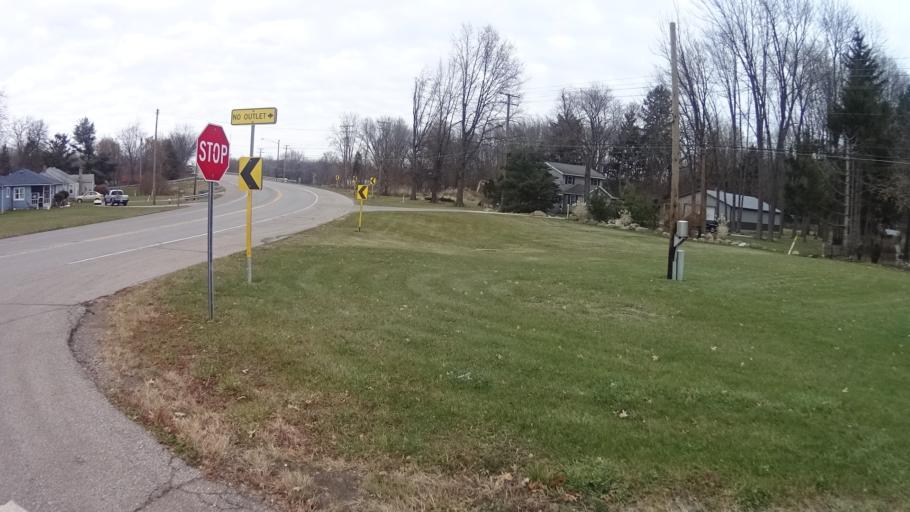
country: US
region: Ohio
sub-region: Lorain County
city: North Ridgeville
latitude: 41.3776
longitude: -82.0190
